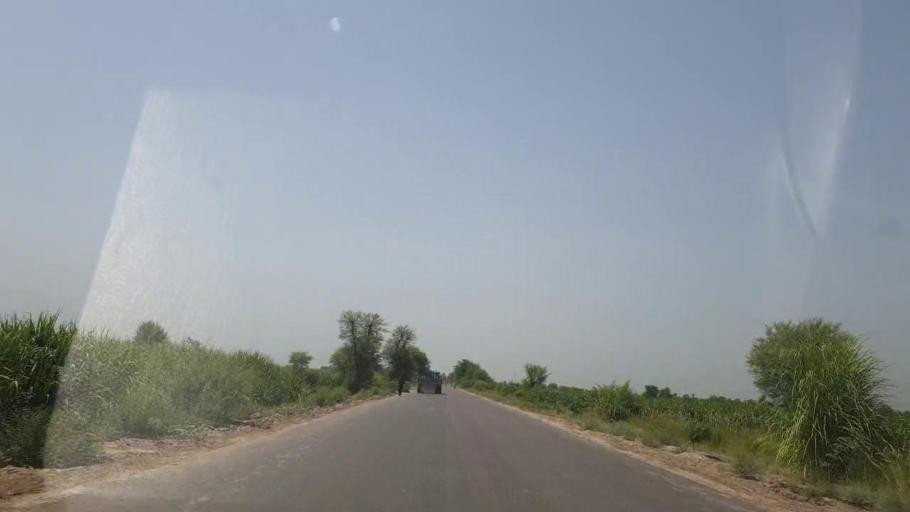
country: PK
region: Sindh
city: Gambat
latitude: 27.2980
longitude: 68.6052
